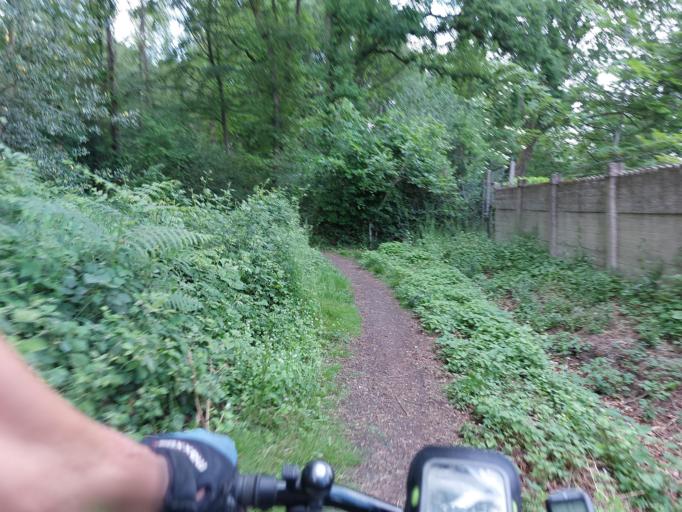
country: BE
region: Wallonia
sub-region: Province du Hainaut
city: Beloeil
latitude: 50.4924
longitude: 3.7599
